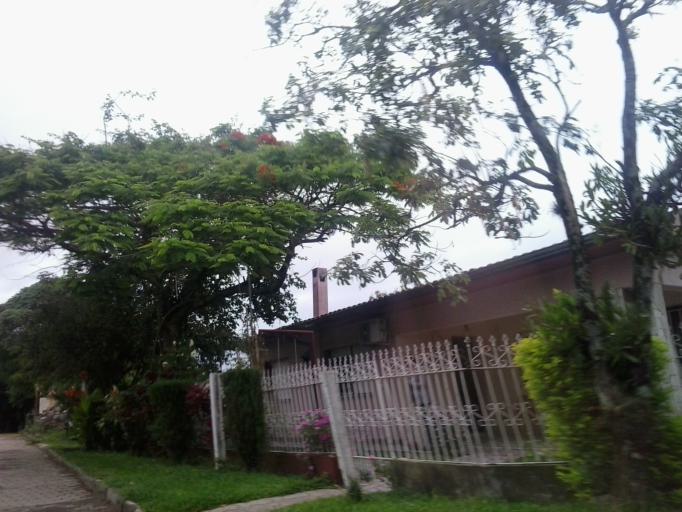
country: BR
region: Rio Grande do Sul
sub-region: Santa Maria
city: Santa Maria
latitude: -29.7227
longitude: -53.3859
